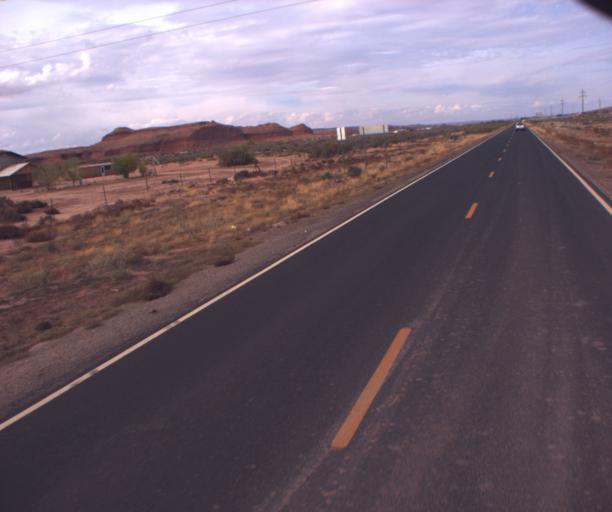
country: US
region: Arizona
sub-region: Apache County
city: Many Farms
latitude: 36.7024
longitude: -109.6177
